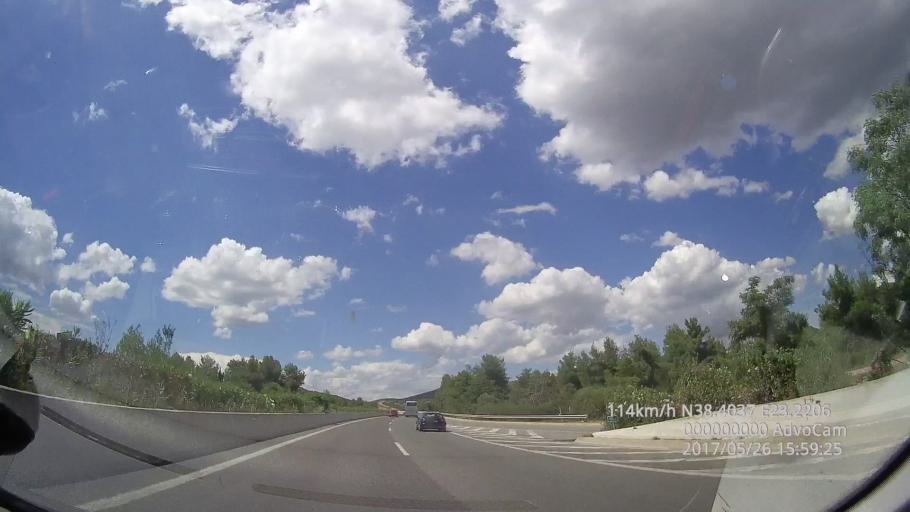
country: GR
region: Central Greece
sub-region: Nomos Fthiotidos
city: Ayios Konstandinos
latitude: 38.7651
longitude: 22.8381
